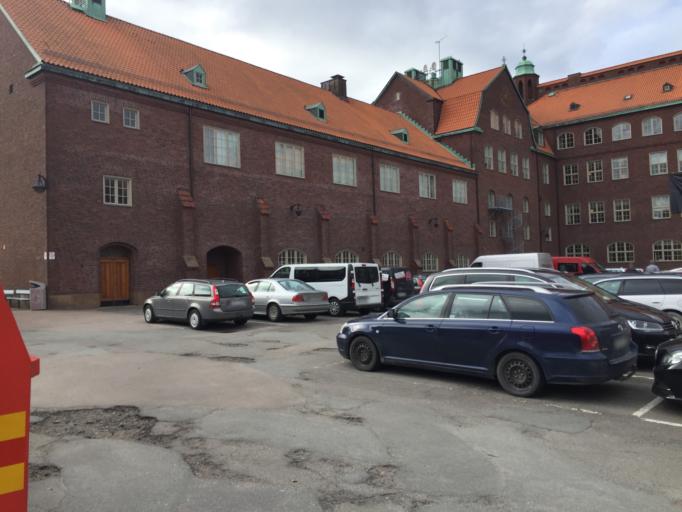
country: SE
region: Vaestra Goetaland
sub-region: Goteborg
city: Goeteborg
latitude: 57.6954
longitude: 11.9748
